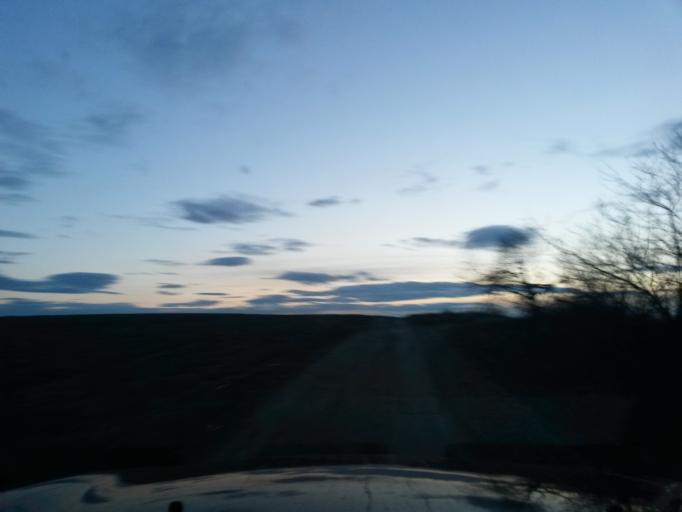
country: SK
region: Kosicky
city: Kosice
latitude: 48.6897
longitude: 21.3792
